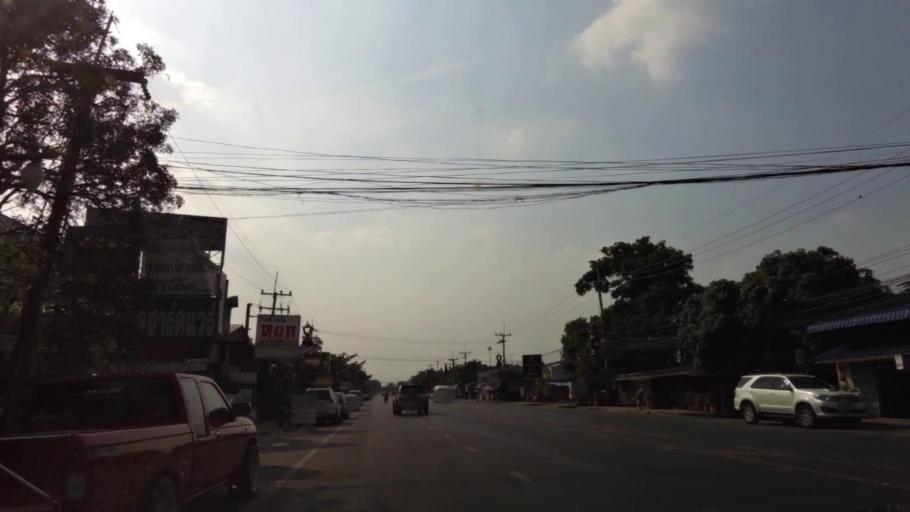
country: TH
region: Phra Nakhon Si Ayutthaya
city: Phra Nakhon Si Ayutthaya
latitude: 14.3441
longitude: 100.5900
